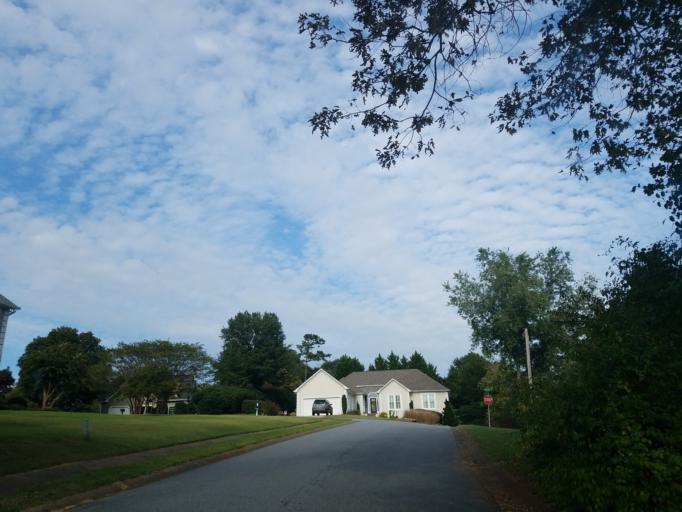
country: US
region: Georgia
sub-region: Cherokee County
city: Woodstock
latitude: 34.0449
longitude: -84.4966
